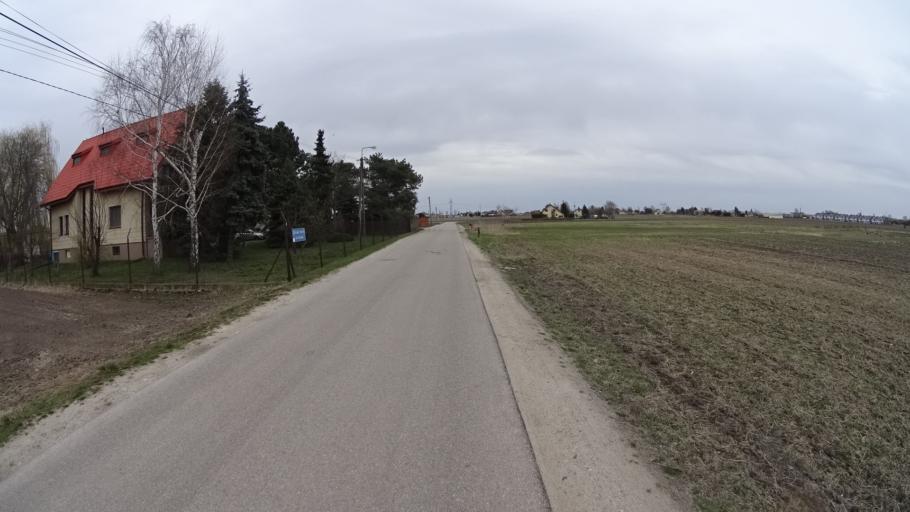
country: PL
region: Masovian Voivodeship
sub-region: Powiat warszawski zachodni
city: Stare Babice
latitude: 52.2426
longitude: 20.8214
